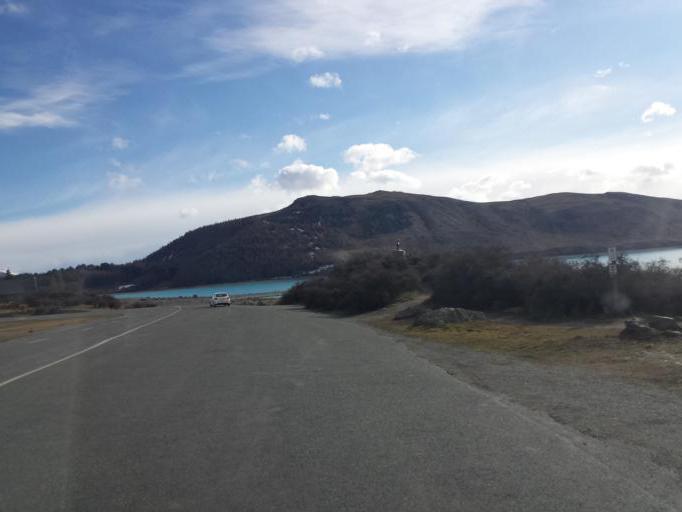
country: NZ
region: Canterbury
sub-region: Timaru District
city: Pleasant Point
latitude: -44.0039
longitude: 170.4844
